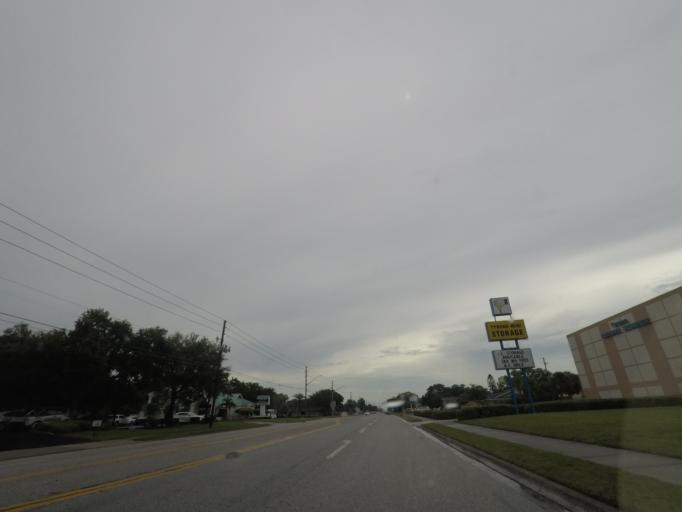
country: US
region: Florida
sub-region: Pinellas County
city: Kenneth City
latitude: 27.8063
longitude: -82.7455
